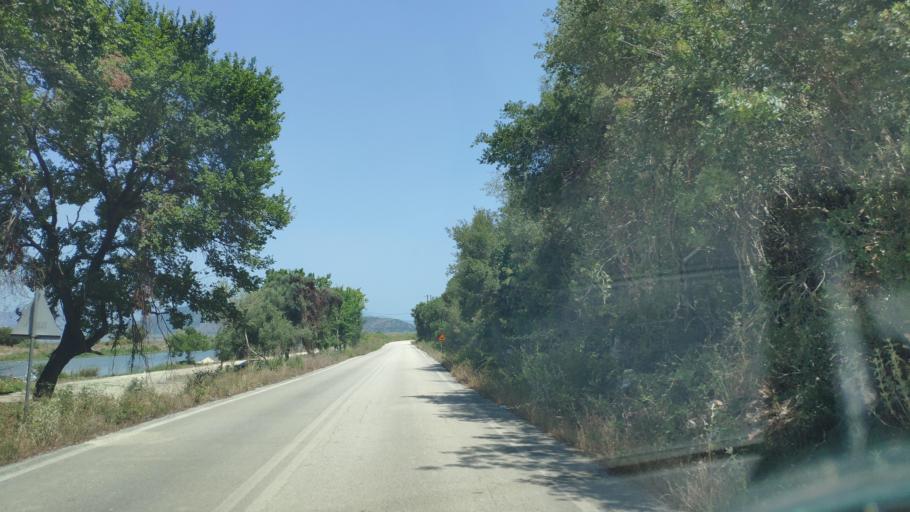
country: GR
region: Epirus
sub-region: Nomos Artas
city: Aneza
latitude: 39.0378
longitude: 20.8596
